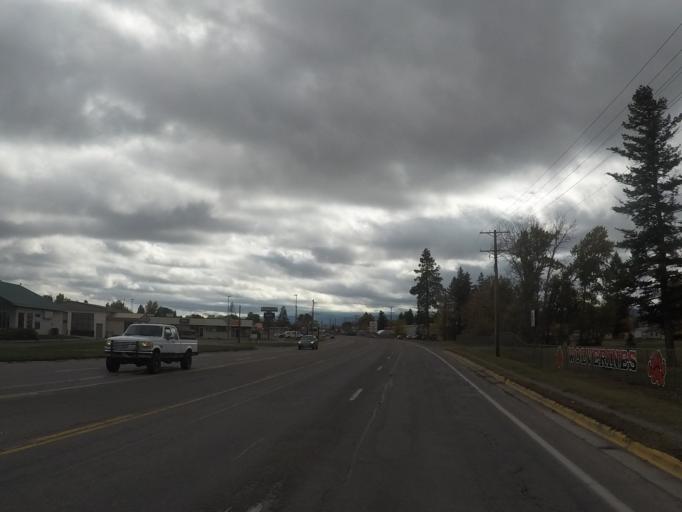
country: US
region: Montana
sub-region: Flathead County
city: Evergreen
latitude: 48.2249
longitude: -114.2768
